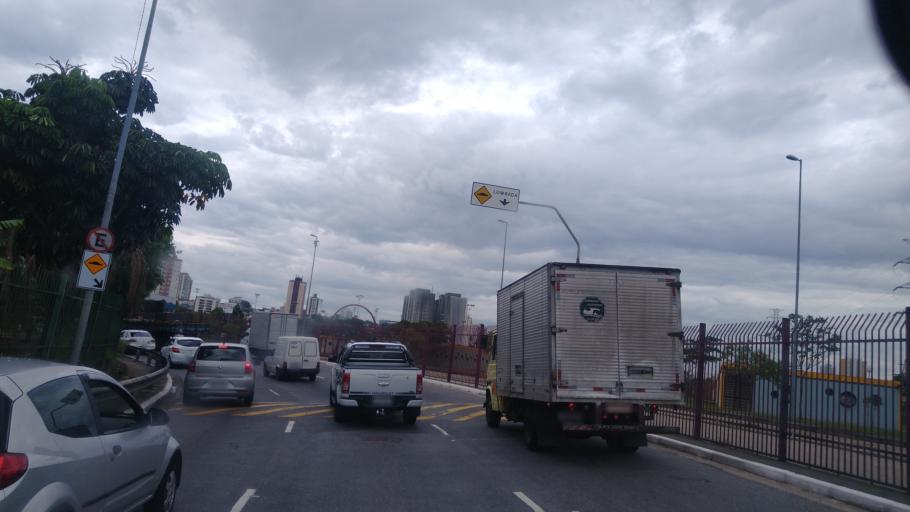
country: BR
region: Sao Paulo
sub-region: Guarulhos
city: Guarulhos
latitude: -23.5190
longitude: -46.5591
